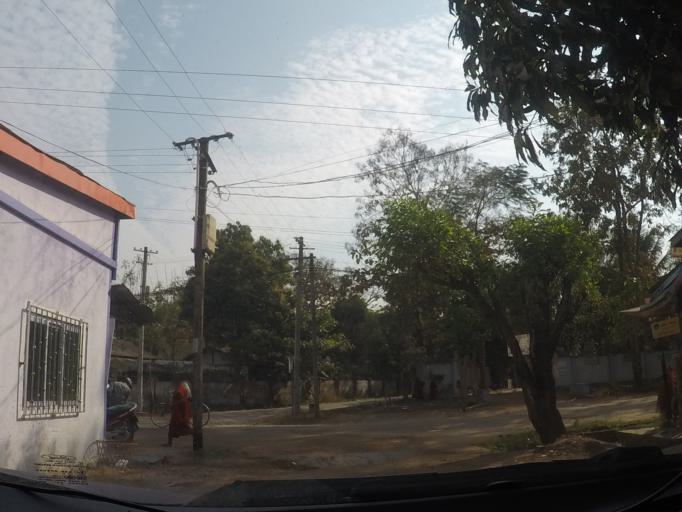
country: MM
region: Bago
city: Pyay
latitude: 18.8188
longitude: 95.2449
